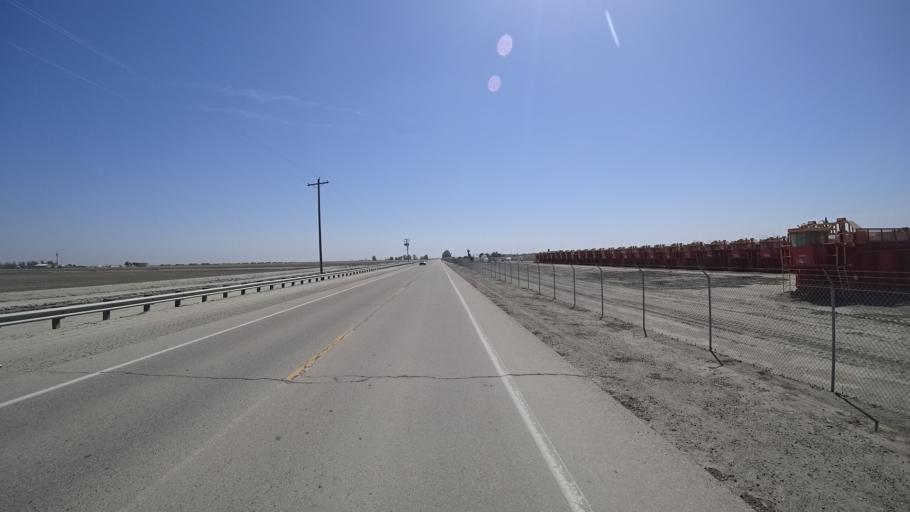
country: US
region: California
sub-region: Kings County
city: Corcoran
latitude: 36.0651
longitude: -119.5650
